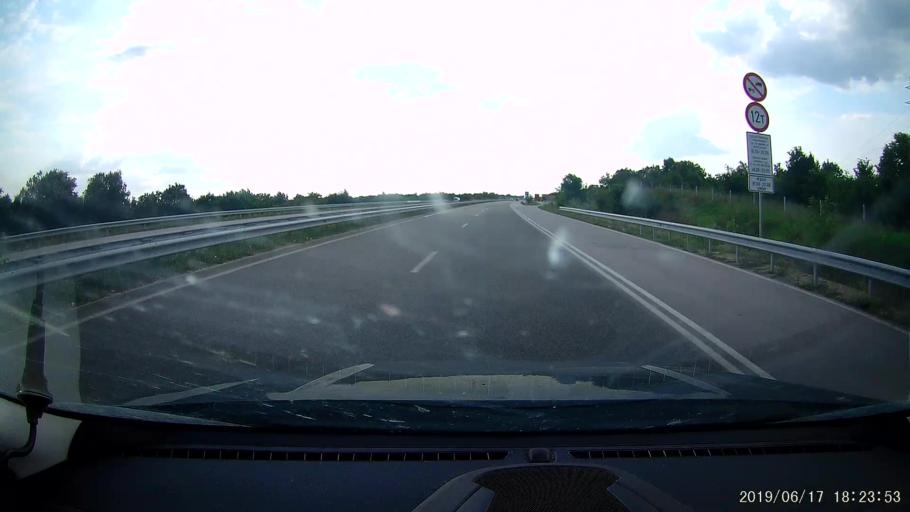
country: BG
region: Khaskovo
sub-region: Obshtina Dimitrovgrad
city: Dimitrovgrad
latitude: 41.9784
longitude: 25.7073
